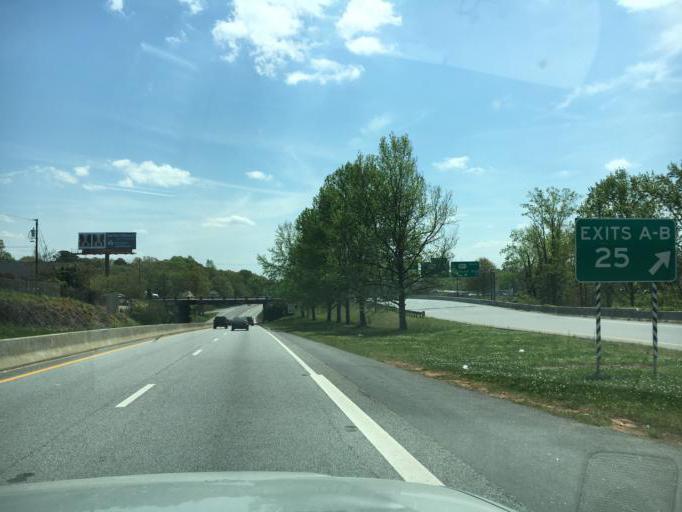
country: US
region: South Carolina
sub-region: Spartanburg County
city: Saxon
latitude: 34.9759
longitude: -81.9437
